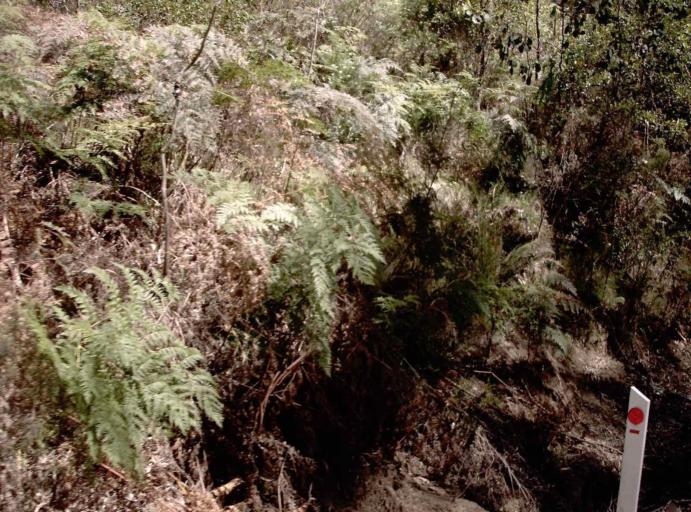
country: AU
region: Victoria
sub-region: East Gippsland
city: Lakes Entrance
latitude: -37.2249
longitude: 148.2637
